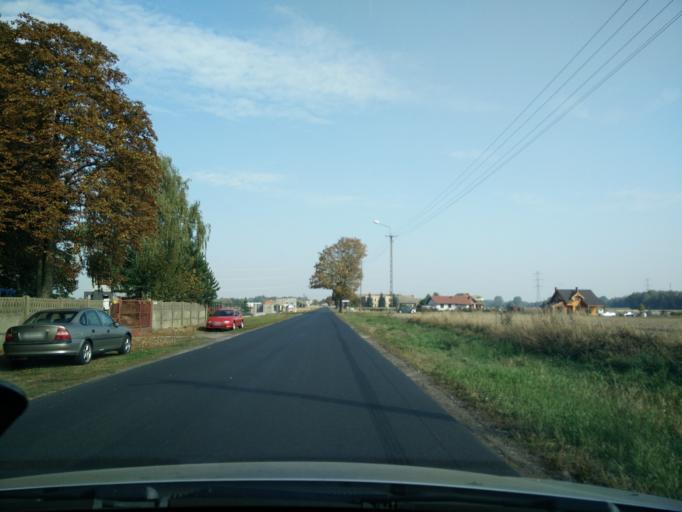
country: PL
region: Greater Poland Voivodeship
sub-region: Powiat sredzki
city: Dominowo
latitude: 52.2946
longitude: 17.3366
